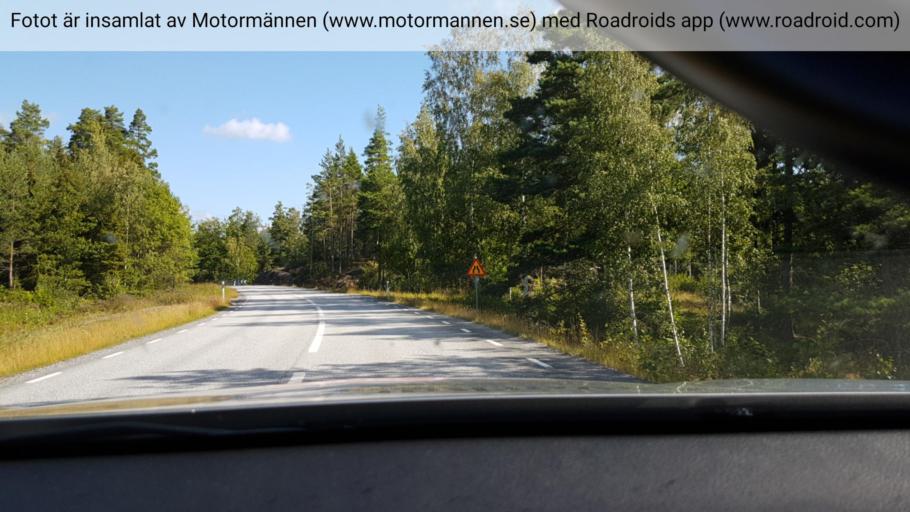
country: SE
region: Stockholm
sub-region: Norrtalje Kommun
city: Norrtalje
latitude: 59.6715
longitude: 18.8404
